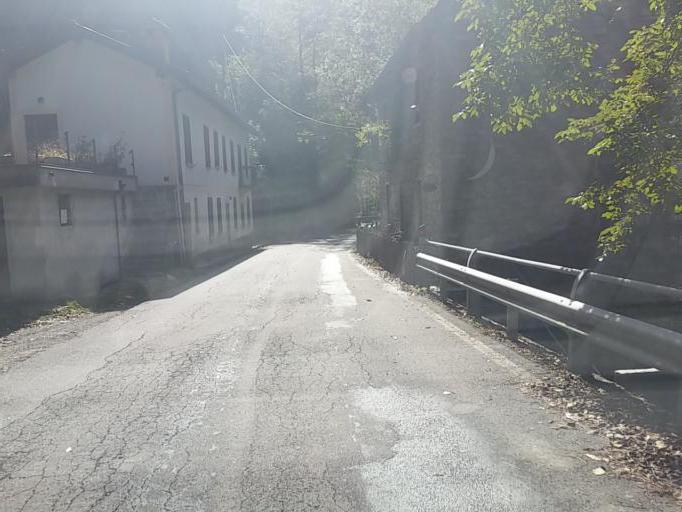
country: IT
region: Piedmont
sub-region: Provincia Verbano-Cusio-Ossola
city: Falmenta
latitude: 46.0906
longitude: 8.5933
